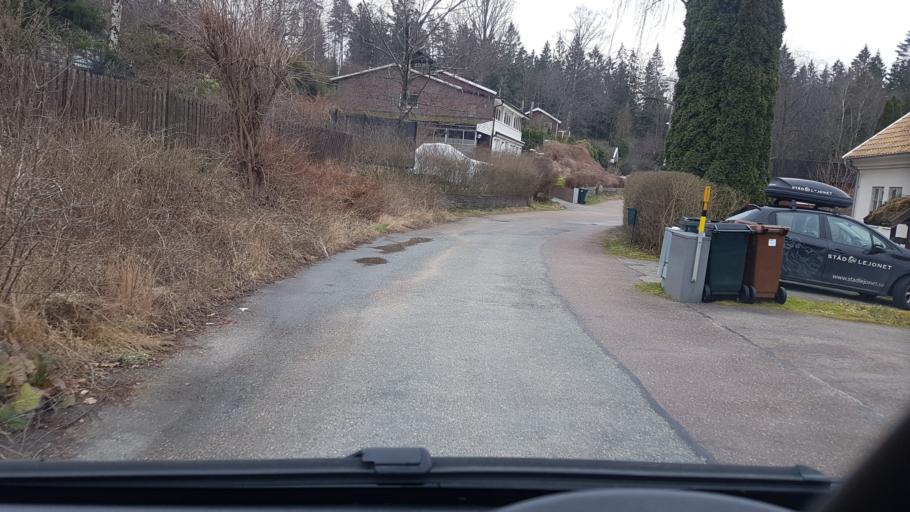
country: SE
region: Vaestra Goetaland
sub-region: Lerums Kommun
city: Stenkullen
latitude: 57.7962
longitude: 12.3651
